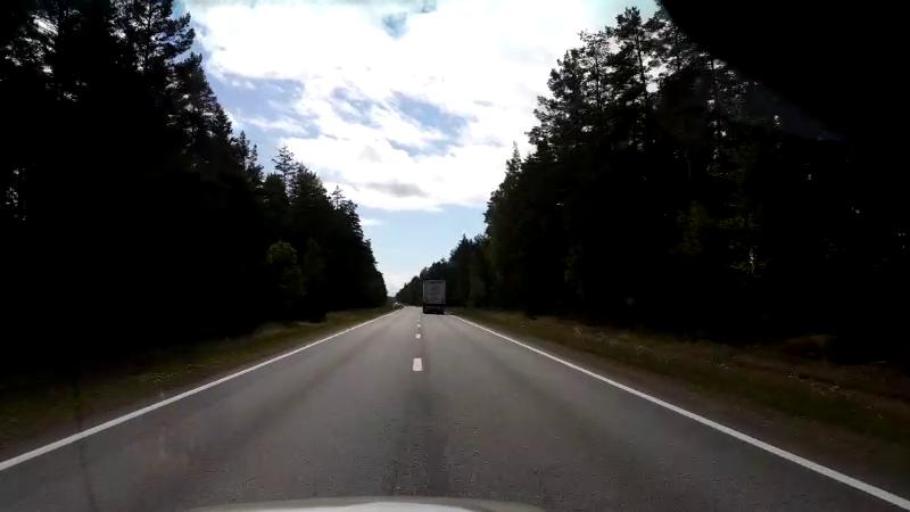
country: LV
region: Salacgrivas
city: Salacgriva
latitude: 57.5283
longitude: 24.4308
